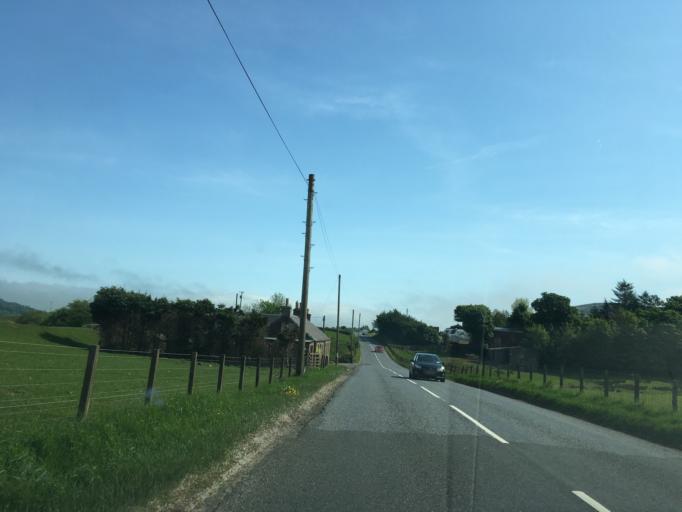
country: GB
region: Scotland
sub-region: The Scottish Borders
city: West Linton
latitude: 55.6728
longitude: -3.4146
